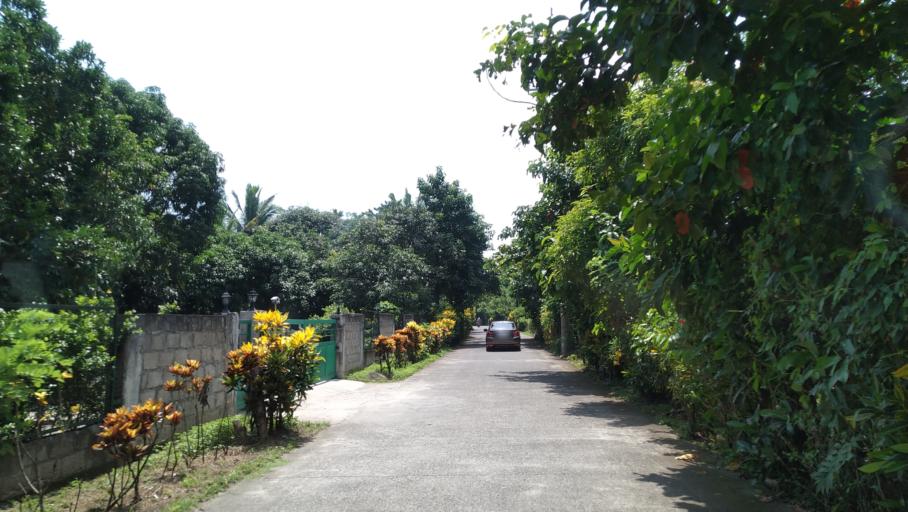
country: PH
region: Calabarzon
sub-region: Province of Laguna
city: Cabanbanan
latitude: 14.2421
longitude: 121.4153
